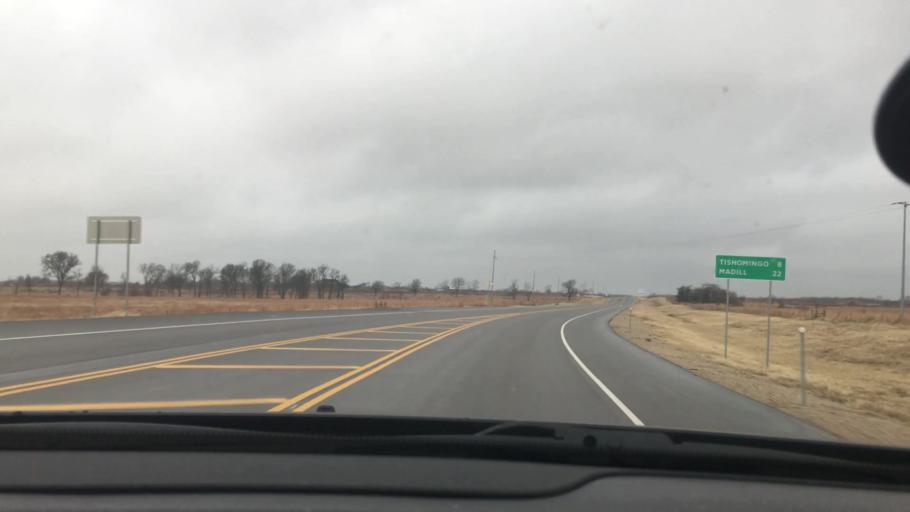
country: US
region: Oklahoma
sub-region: Johnston County
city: Tishomingo
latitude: 34.3459
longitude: -96.6372
